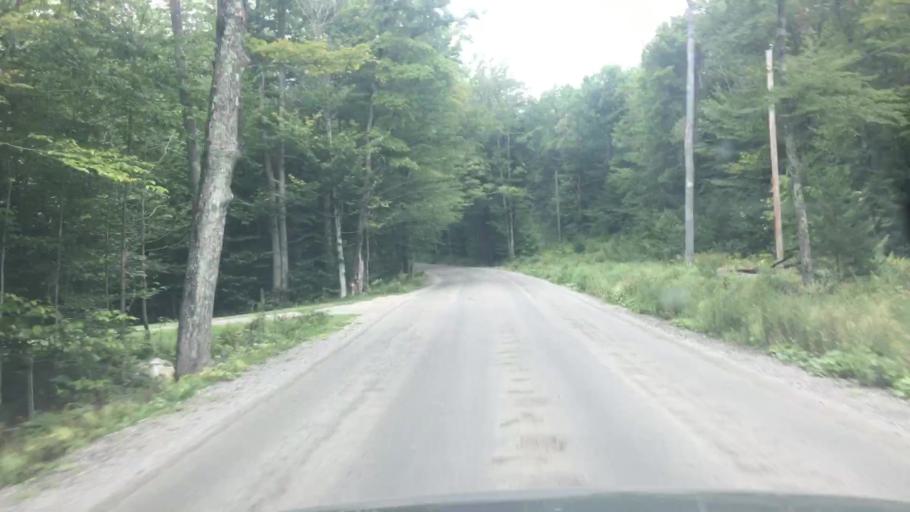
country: US
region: Vermont
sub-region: Windham County
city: Dover
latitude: 42.8246
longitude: -72.7944
